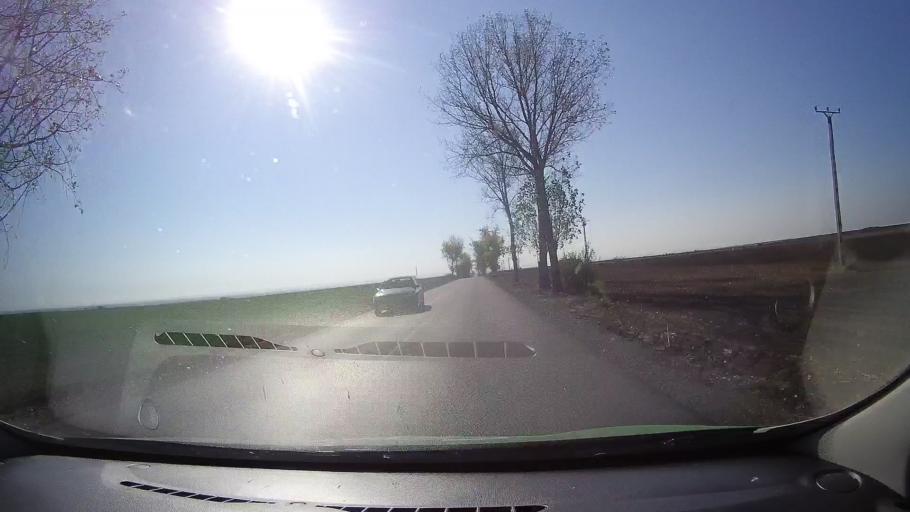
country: RO
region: Satu Mare
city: Carei
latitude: 47.6548
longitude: 22.4610
